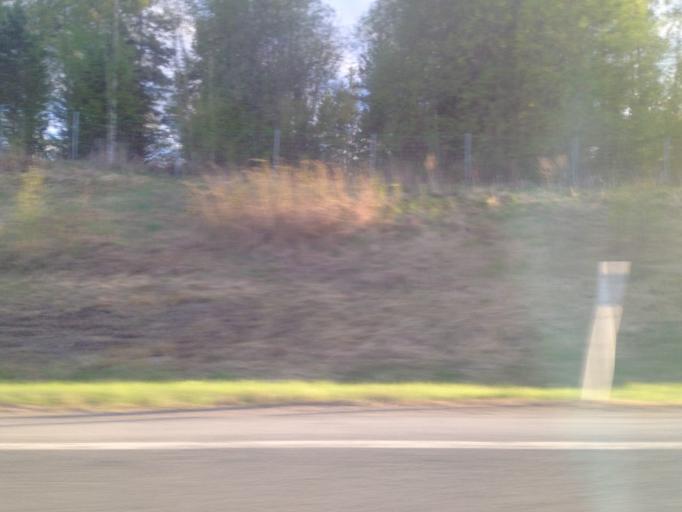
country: FI
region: Pirkanmaa
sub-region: Etelae-Pirkanmaa
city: Akaa
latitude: 61.1601
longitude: 23.9649
